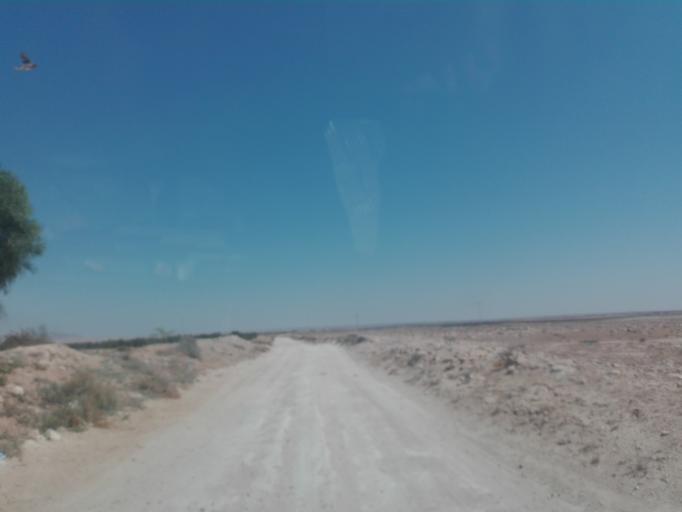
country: TN
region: Safaqis
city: Skhira
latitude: 34.3709
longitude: 9.9068
